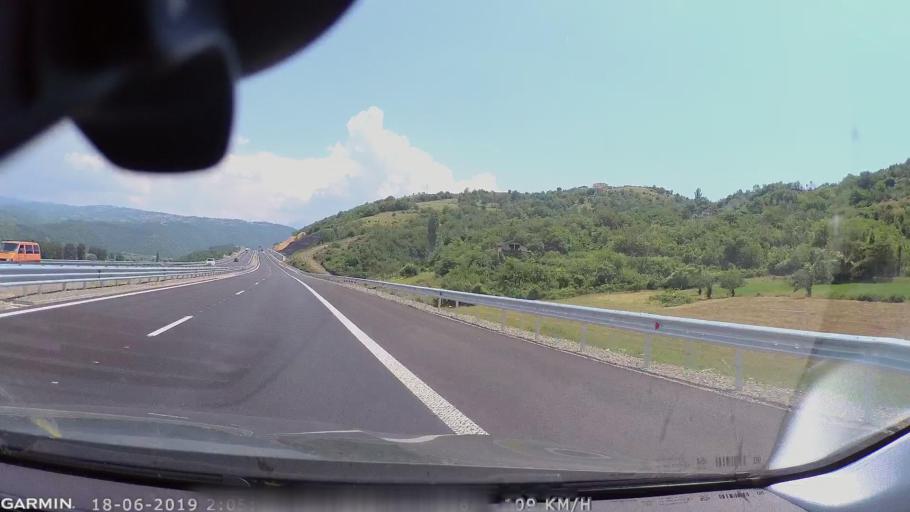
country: BG
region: Blagoevgrad
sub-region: Obshtina Blagoevgrad
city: Blagoevgrad
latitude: 41.9779
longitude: 23.0677
